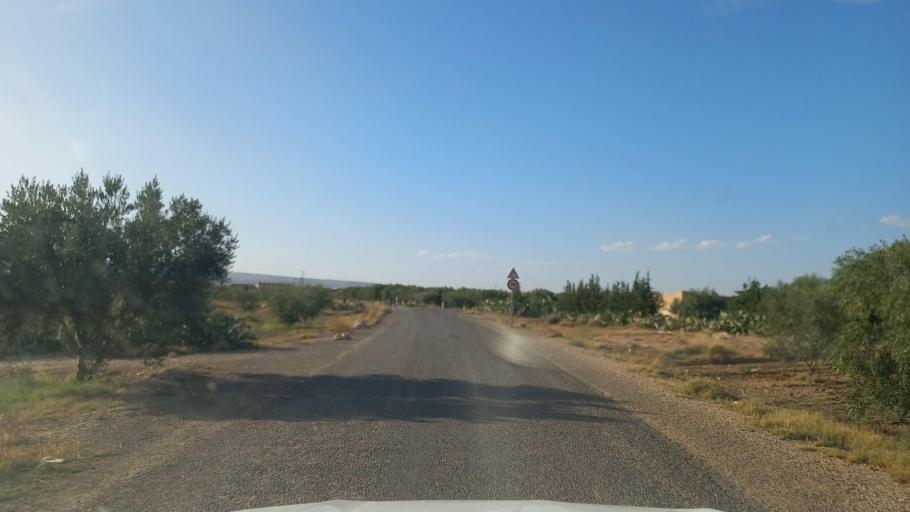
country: TN
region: Al Qasrayn
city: Kasserine
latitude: 35.2659
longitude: 9.0277
